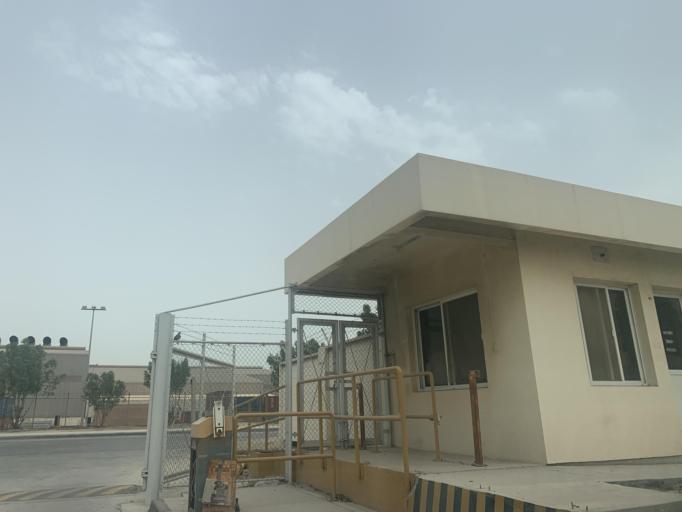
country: BH
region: Northern
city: Sitrah
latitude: 26.1792
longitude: 50.6144
